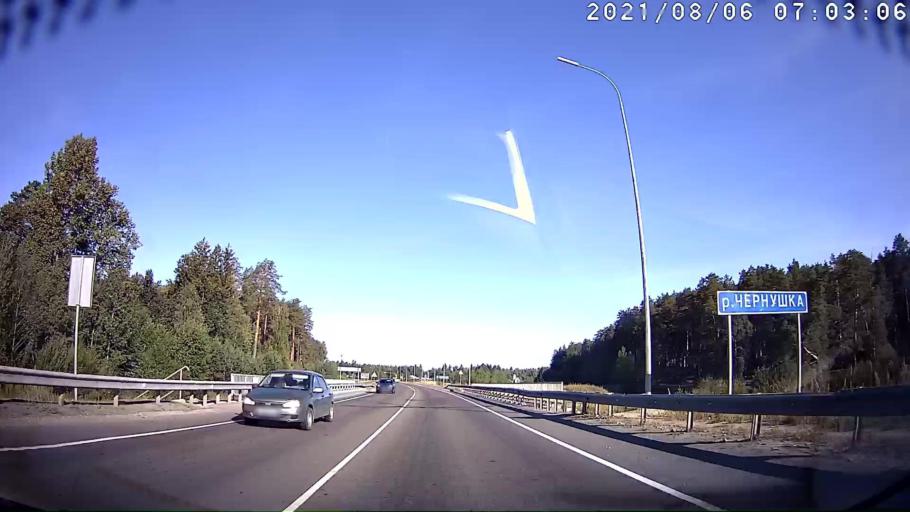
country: RU
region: Mariy-El
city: Yoshkar-Ola
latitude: 56.5396
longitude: 47.9858
